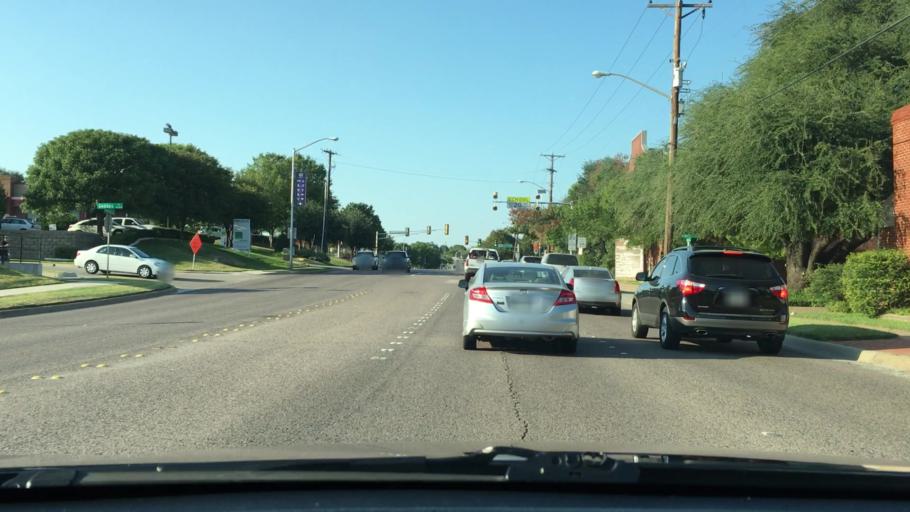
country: US
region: Texas
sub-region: Tarrant County
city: Westworth
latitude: 32.7277
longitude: -97.3878
